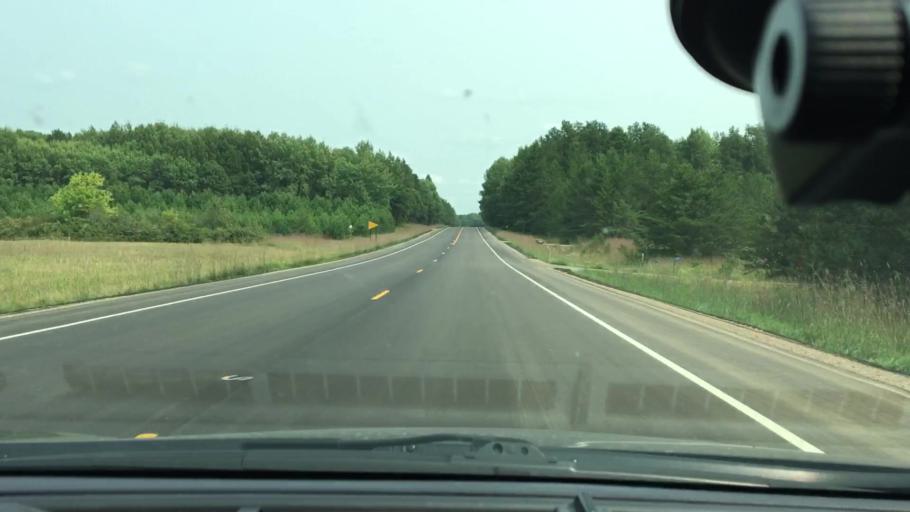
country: US
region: Minnesota
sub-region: Crow Wing County
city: Nisswa
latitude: 46.5296
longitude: -94.2419
